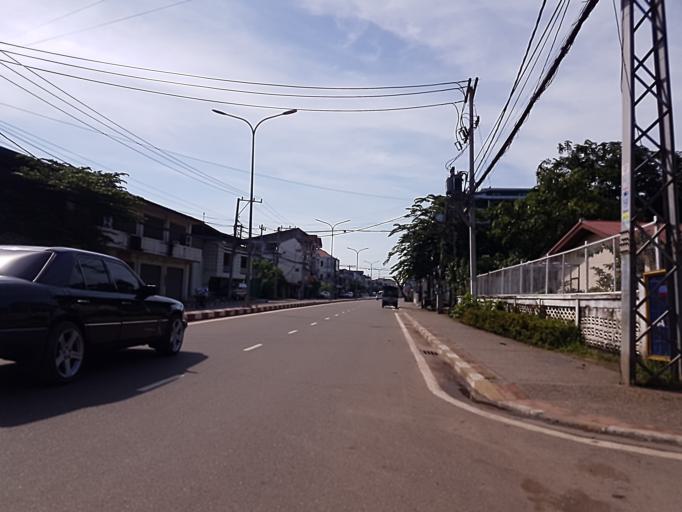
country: LA
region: Vientiane
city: Vientiane
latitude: 17.9556
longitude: 102.6181
